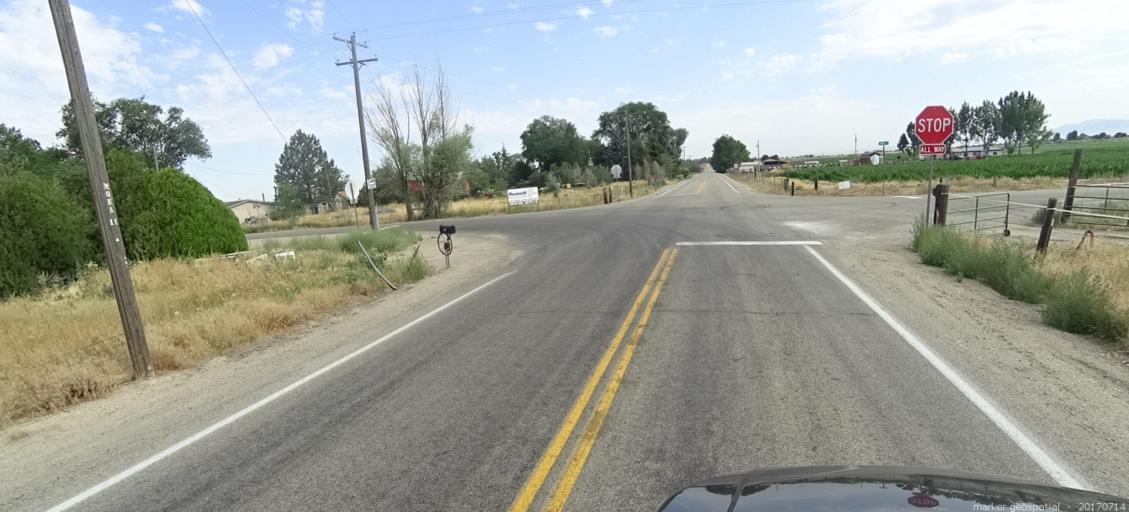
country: US
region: Idaho
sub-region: Ada County
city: Kuna
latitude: 43.4734
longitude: -116.3545
